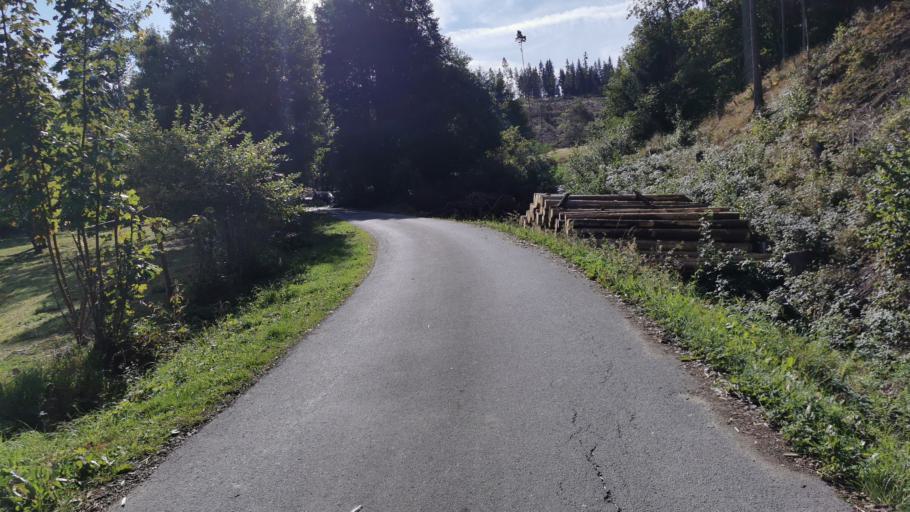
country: DE
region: Bavaria
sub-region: Upper Franconia
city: Ludwigsstadt
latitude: 50.4811
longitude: 11.4136
